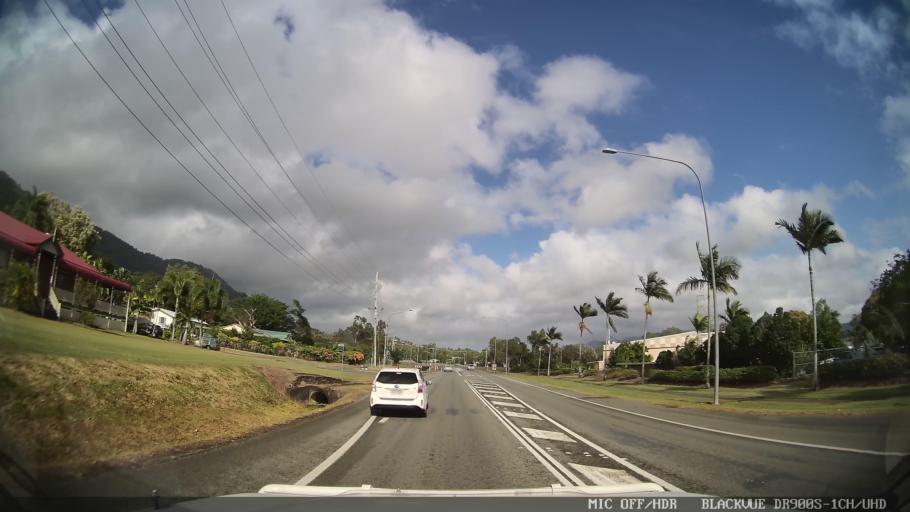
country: AU
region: Queensland
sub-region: Whitsunday
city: Proserpine
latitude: -20.2725
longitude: 148.7056
